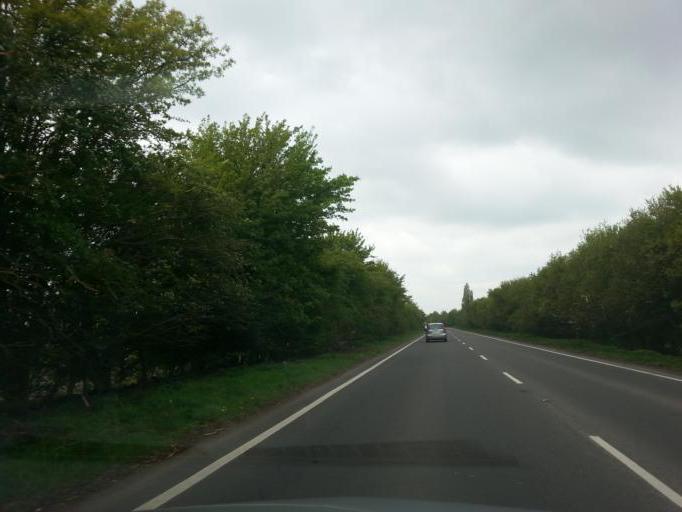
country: GB
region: England
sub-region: Norfolk
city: Emneth
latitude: 52.6285
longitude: 0.2066
